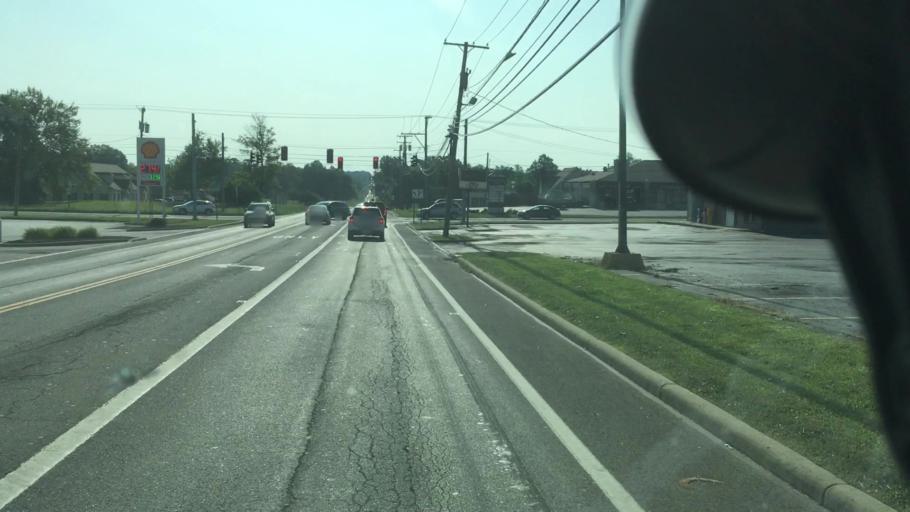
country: US
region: Ohio
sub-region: Mahoning County
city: Poland
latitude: 41.0237
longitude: -80.5924
